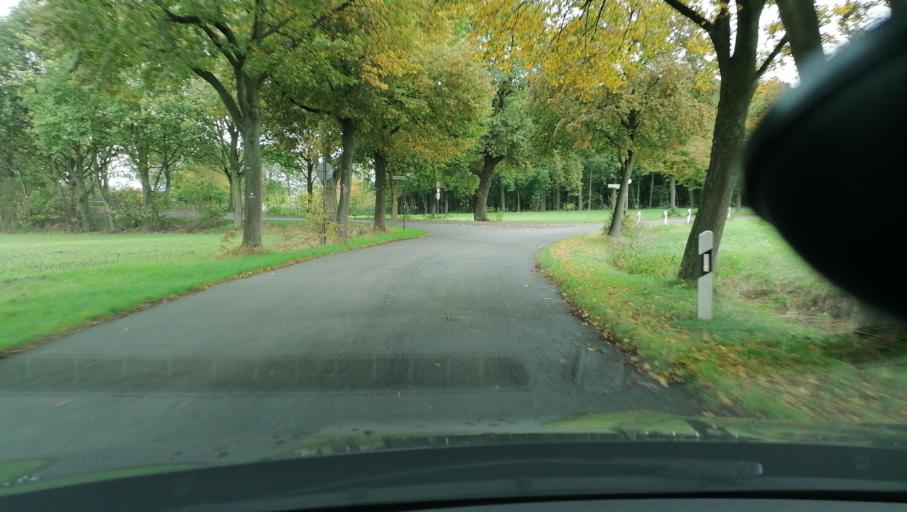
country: DE
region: North Rhine-Westphalia
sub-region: Regierungsbezirk Munster
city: Recklinghausen
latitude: 51.6361
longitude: 7.1728
